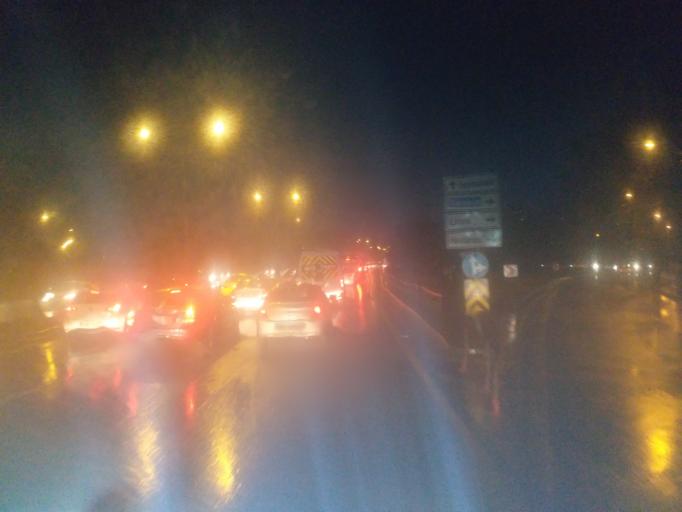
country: TR
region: Ankara
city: Ankara
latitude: 39.9527
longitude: 32.8221
